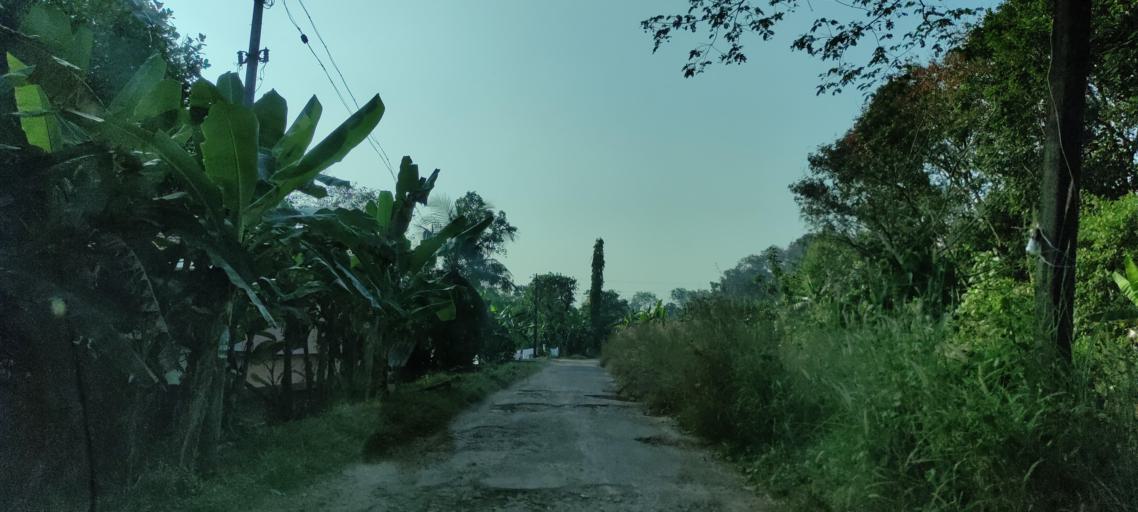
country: IN
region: Kerala
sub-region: Pattanamtitta
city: Adur
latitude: 9.1354
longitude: 76.7316
